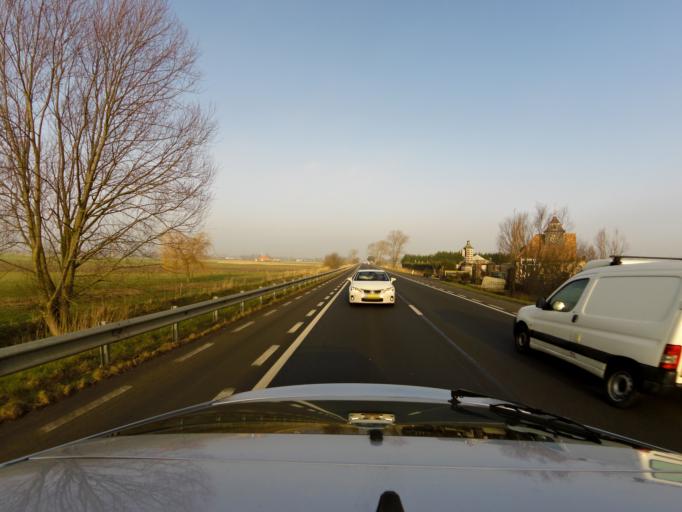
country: BE
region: Flanders
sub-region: Provincie West-Vlaanderen
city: Gistel
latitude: 51.1422
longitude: 2.9657
